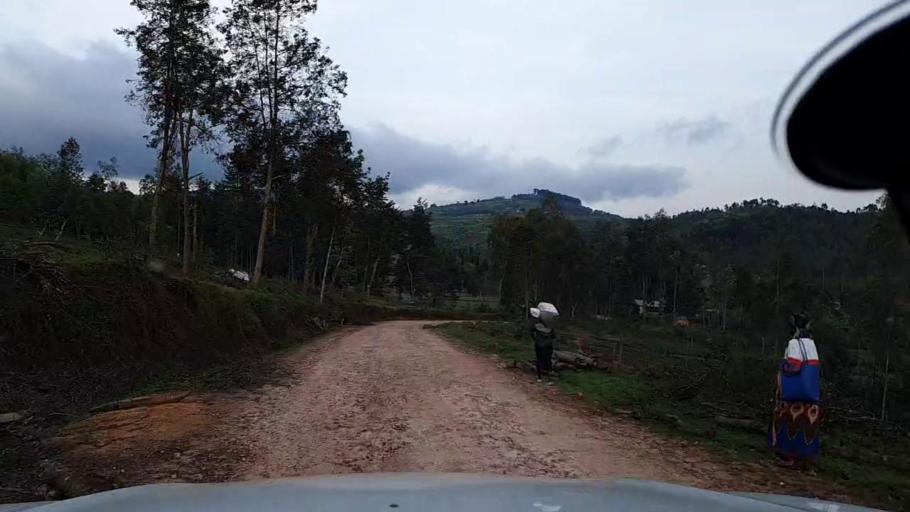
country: RW
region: Southern Province
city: Nyanza
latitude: -2.2103
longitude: 29.6131
